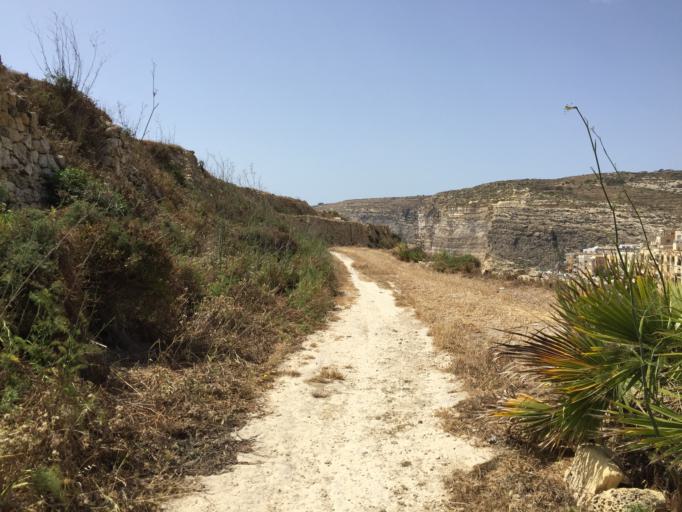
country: MT
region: Il-Munxar
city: Munxar
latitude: 36.0252
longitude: 14.2186
